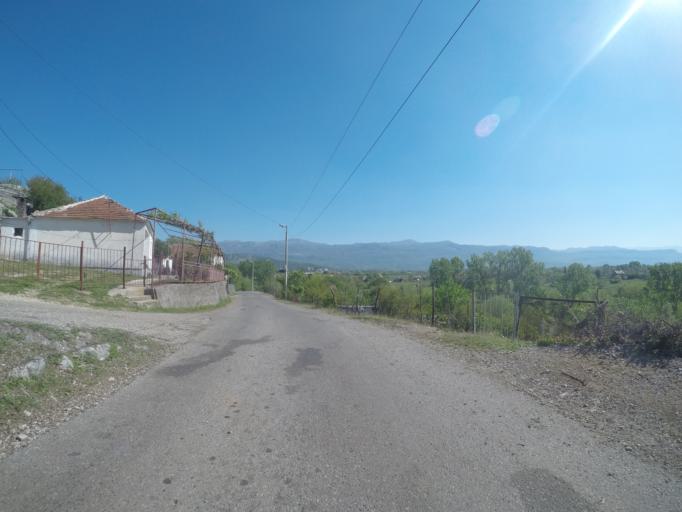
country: ME
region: Danilovgrad
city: Danilovgrad
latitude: 42.5353
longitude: 19.0904
